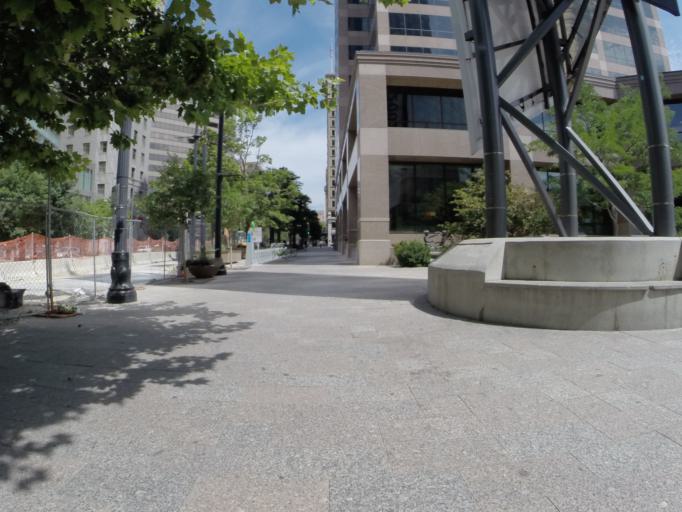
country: US
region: Utah
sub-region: Salt Lake County
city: Salt Lake City
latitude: 40.7640
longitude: -111.8910
